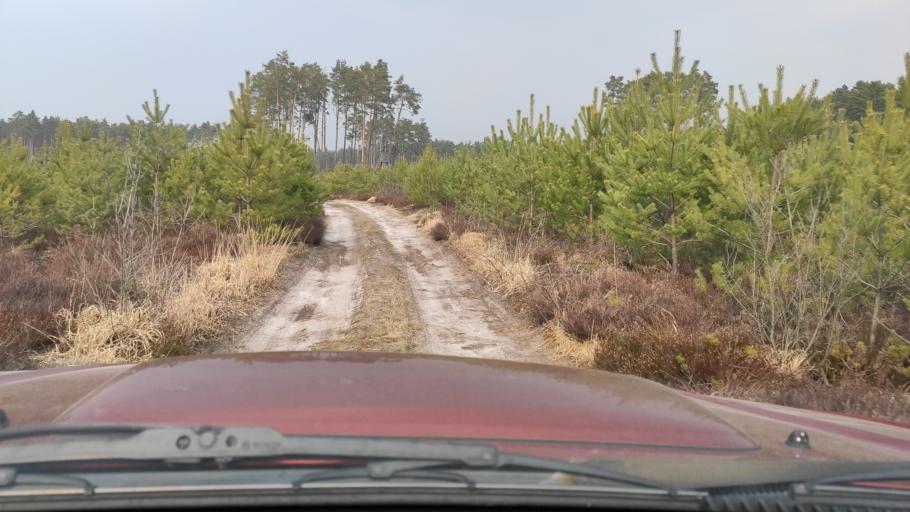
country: PL
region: Masovian Voivodeship
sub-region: Powiat zwolenski
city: Zwolen
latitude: 51.3922
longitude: 21.5723
